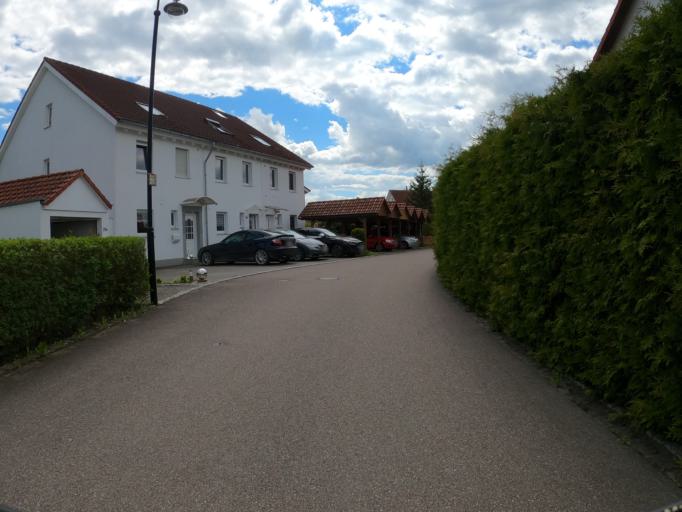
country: DE
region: Bavaria
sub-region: Swabia
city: Leipheim
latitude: 48.4574
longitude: 10.2147
